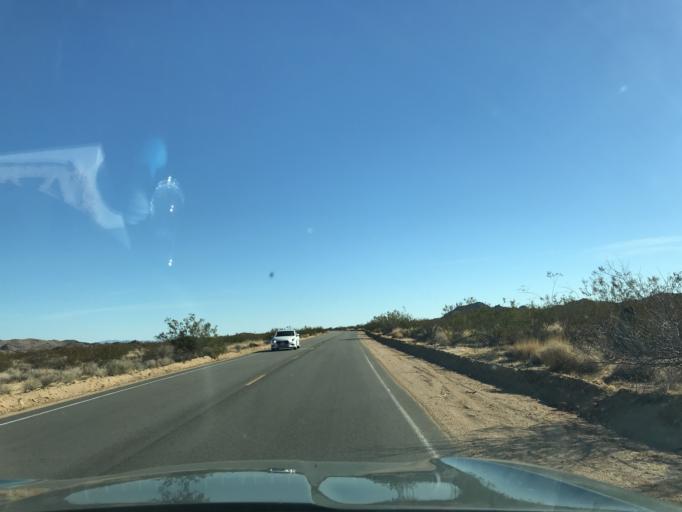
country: US
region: California
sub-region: Riverside County
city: Mecca
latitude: 33.7621
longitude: -115.8167
